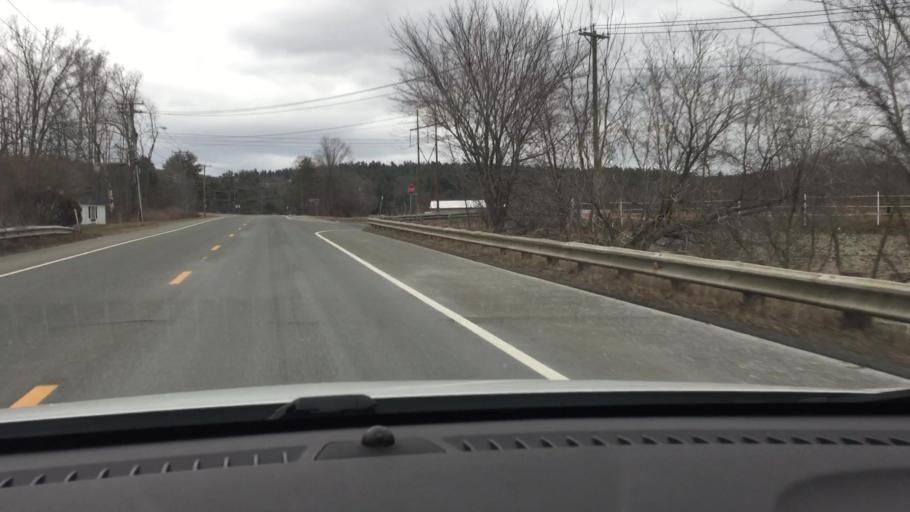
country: US
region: Massachusetts
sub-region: Berkshire County
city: Dalton
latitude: 42.4891
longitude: -73.1266
